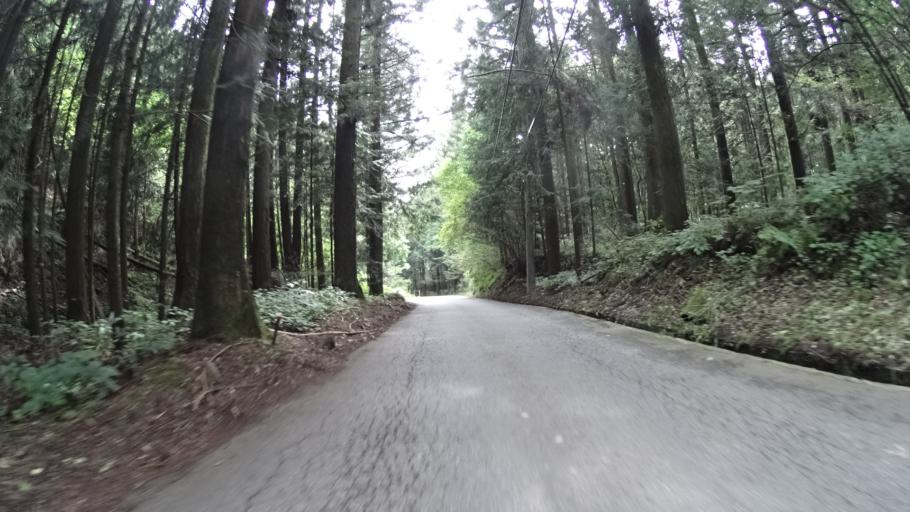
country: JP
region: Yamanashi
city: Nirasaki
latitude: 35.7835
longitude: 138.5351
